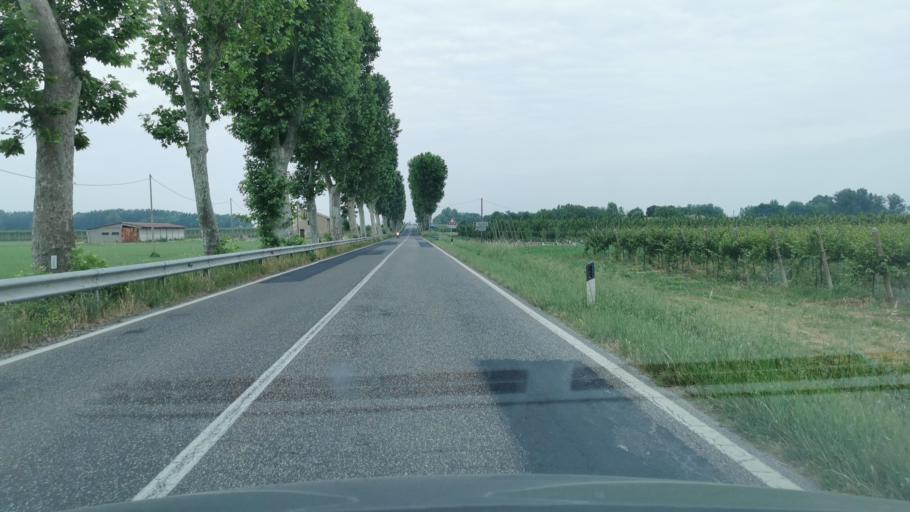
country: IT
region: Emilia-Romagna
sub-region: Provincia di Ravenna
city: Russi
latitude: 44.3989
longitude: 12.0302
